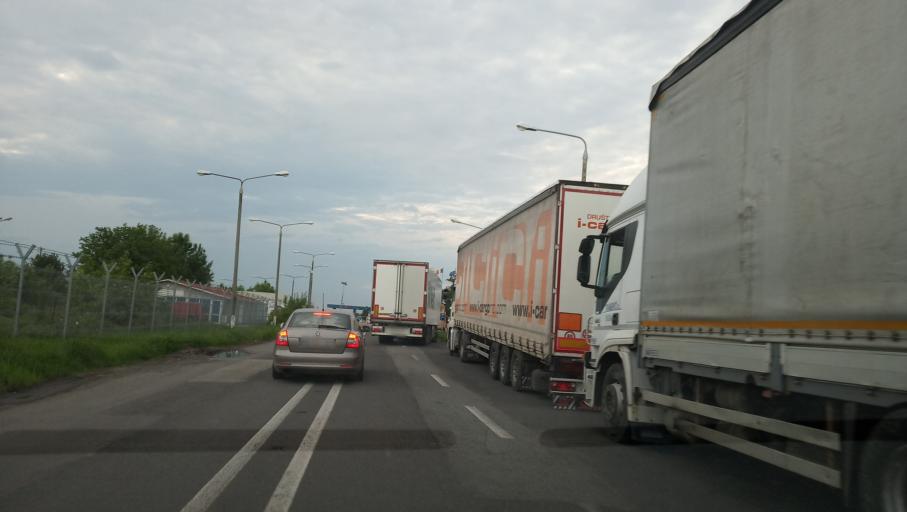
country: RO
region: Timis
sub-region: Comuna Moravita
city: Moravita
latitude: 45.2306
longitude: 21.2741
